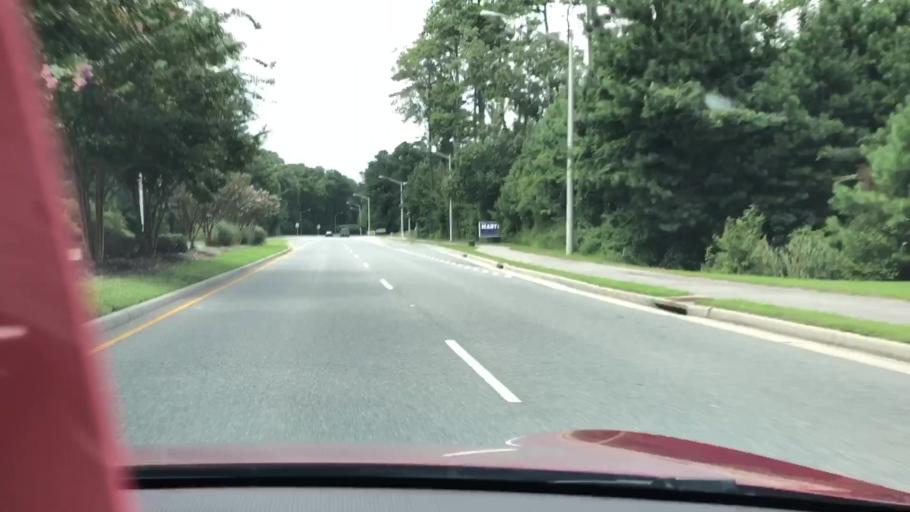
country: US
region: Virginia
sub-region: City of Virginia Beach
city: Virginia Beach
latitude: 36.8146
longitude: -75.9966
